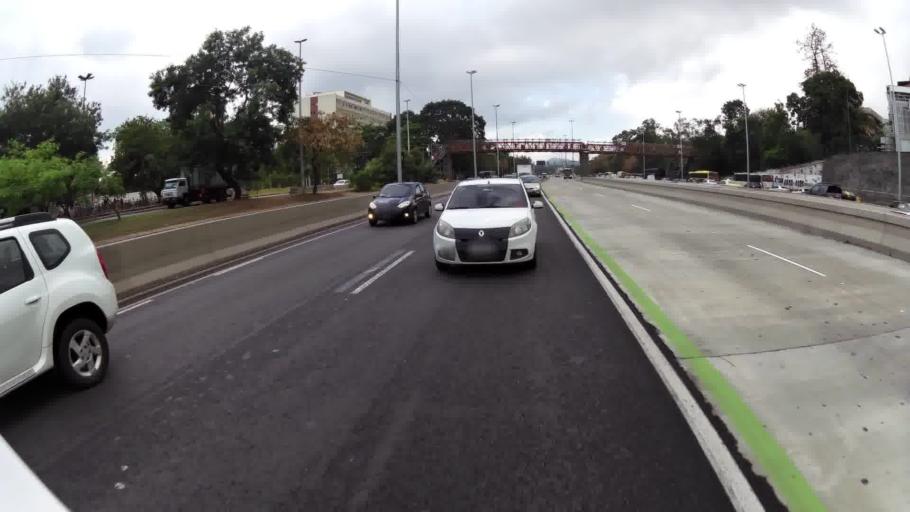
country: BR
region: Rio de Janeiro
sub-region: Rio De Janeiro
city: Rio de Janeiro
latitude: -22.8764
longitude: -43.2420
